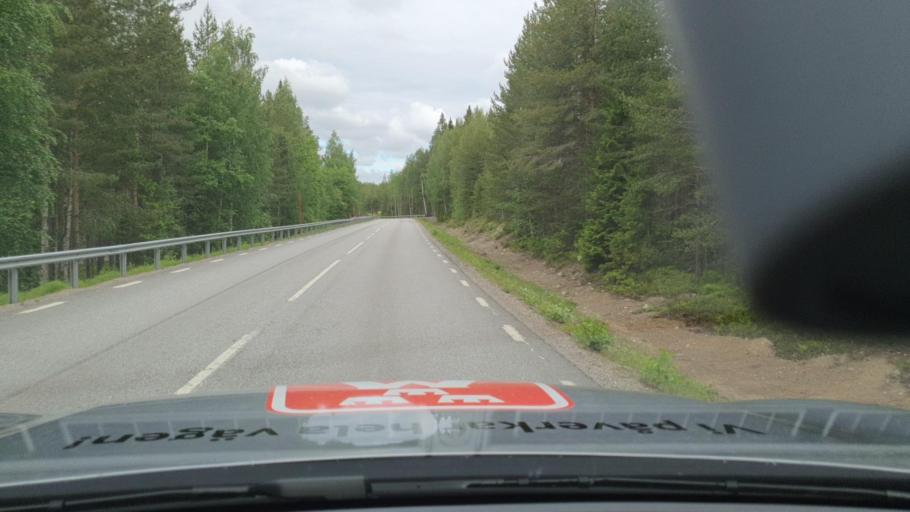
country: SE
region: Norrbotten
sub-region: Lulea Kommun
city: Ranea
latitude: 65.9897
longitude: 22.0423
